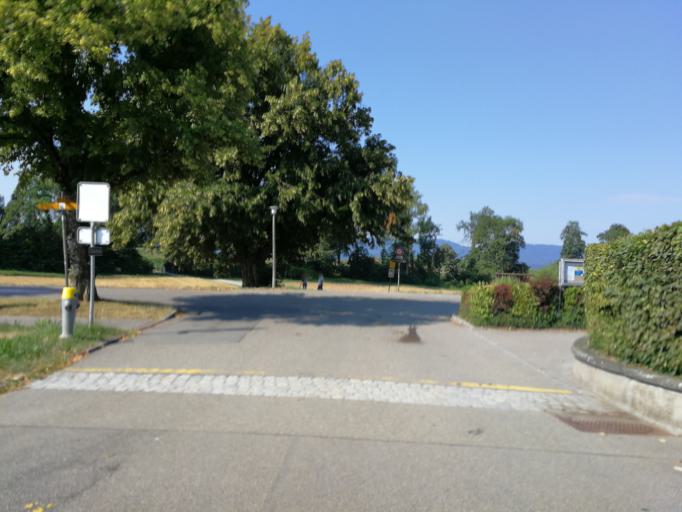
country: CH
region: Zurich
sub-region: Bezirk Meilen
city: Herrliberg
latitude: 47.2967
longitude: 8.6258
